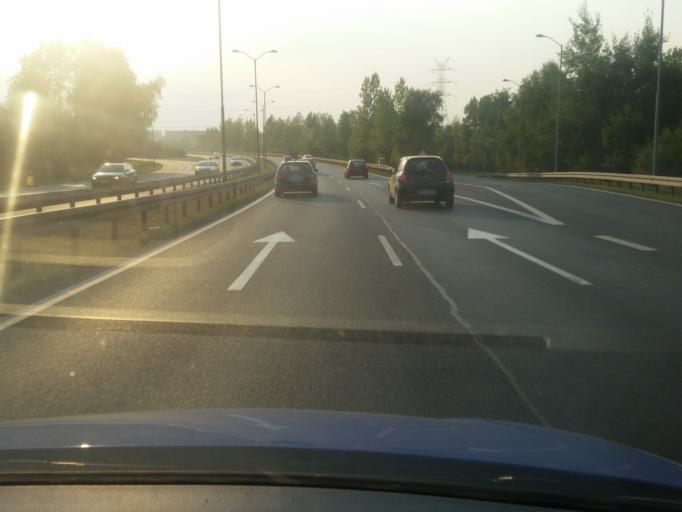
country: PL
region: Silesian Voivodeship
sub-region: Sosnowiec
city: Sosnowiec
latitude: 50.2582
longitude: 19.0773
